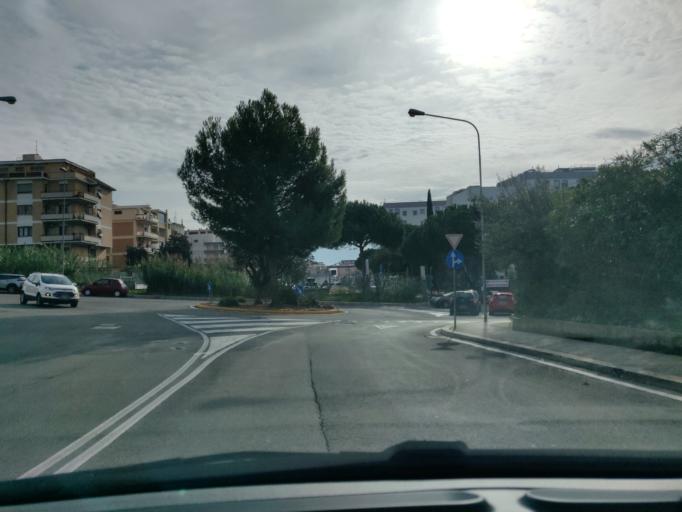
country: IT
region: Latium
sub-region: Citta metropolitana di Roma Capitale
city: Civitavecchia
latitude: 42.0993
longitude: 11.8098
